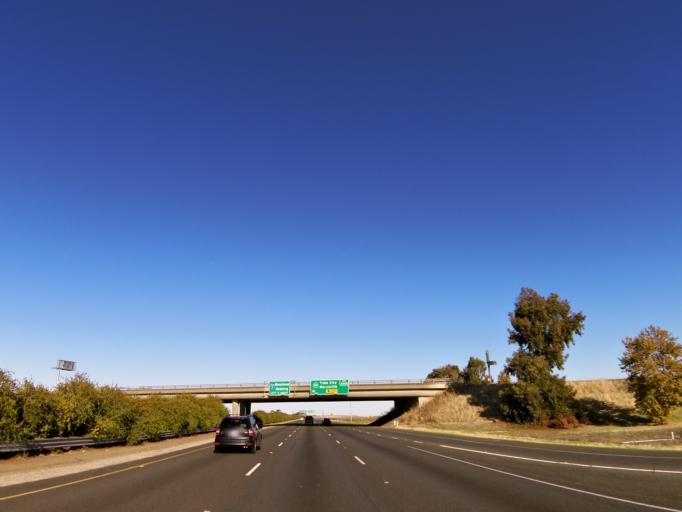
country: US
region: California
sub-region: Yolo County
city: West Sacramento
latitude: 38.6549
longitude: -121.5324
